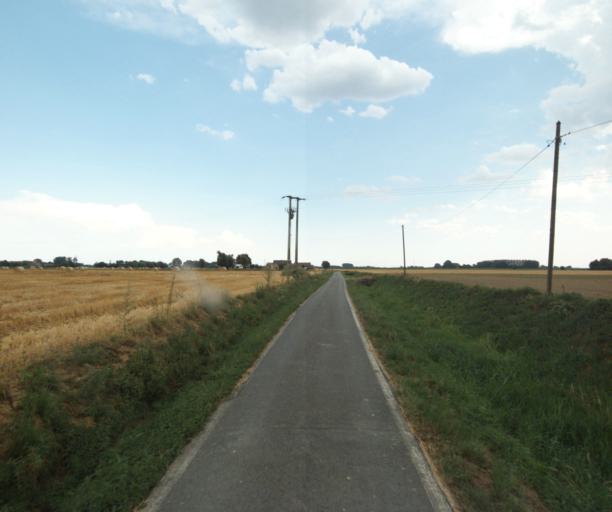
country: FR
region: Nord-Pas-de-Calais
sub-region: Departement du Nord
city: Deulemont
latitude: 50.7456
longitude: 2.9810
